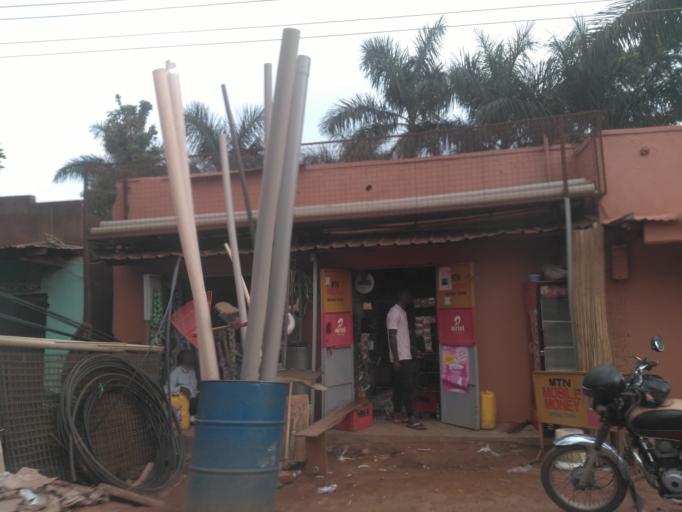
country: UG
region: Central Region
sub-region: Wakiso District
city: Kireka
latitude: 0.3739
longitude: 32.6147
